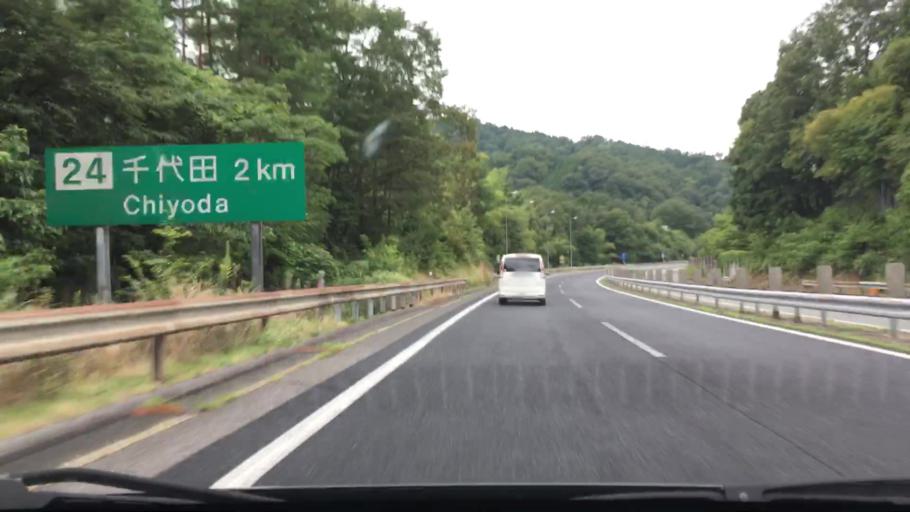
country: JP
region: Hiroshima
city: Hiroshima-shi
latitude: 34.6806
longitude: 132.5612
